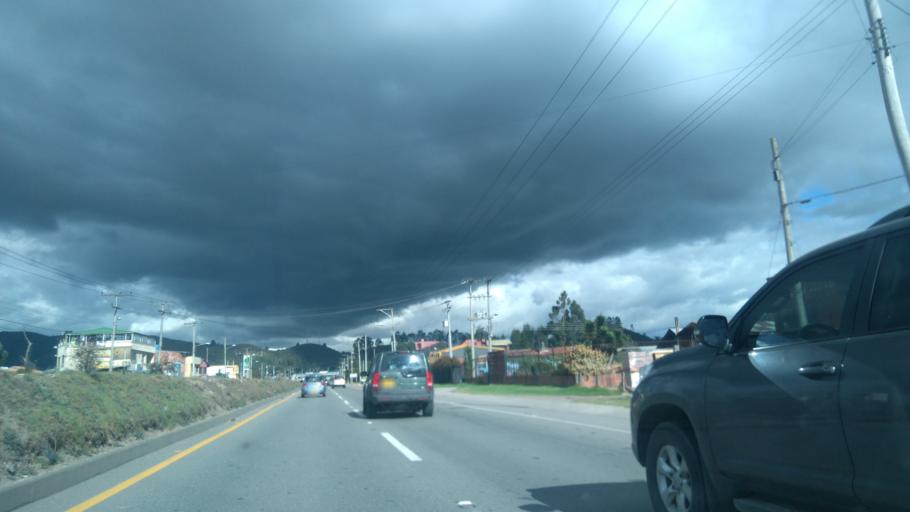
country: CO
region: Cundinamarca
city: El Rosal
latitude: 4.8183
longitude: -74.2276
